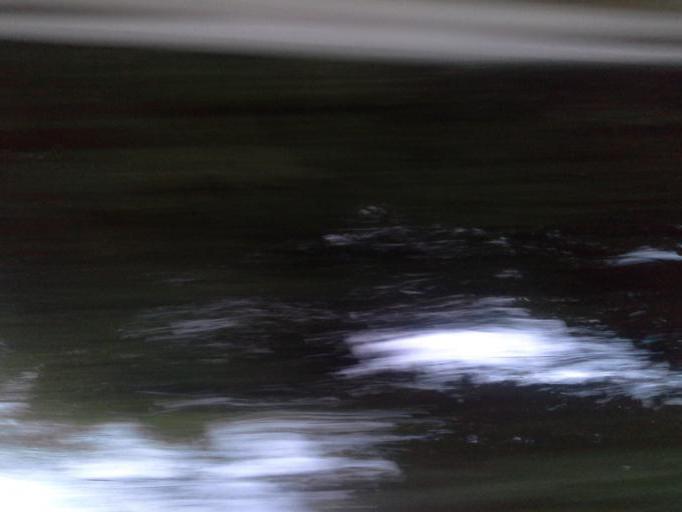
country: CO
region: Sucre
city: Los Palmitos
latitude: 9.3670
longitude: -75.2741
